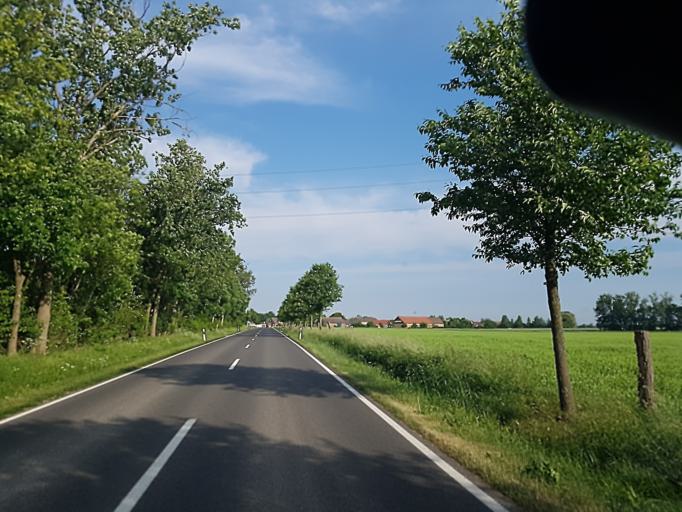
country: DE
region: Saxony-Anhalt
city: Kropstadt
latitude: 52.0205
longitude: 12.7452
